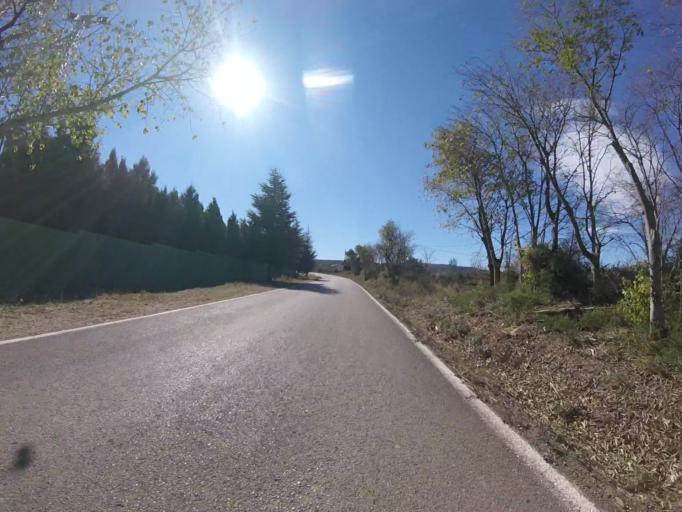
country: ES
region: Valencia
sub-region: Provincia de Castello
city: Albocasser
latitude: 40.3659
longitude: 0.0205
